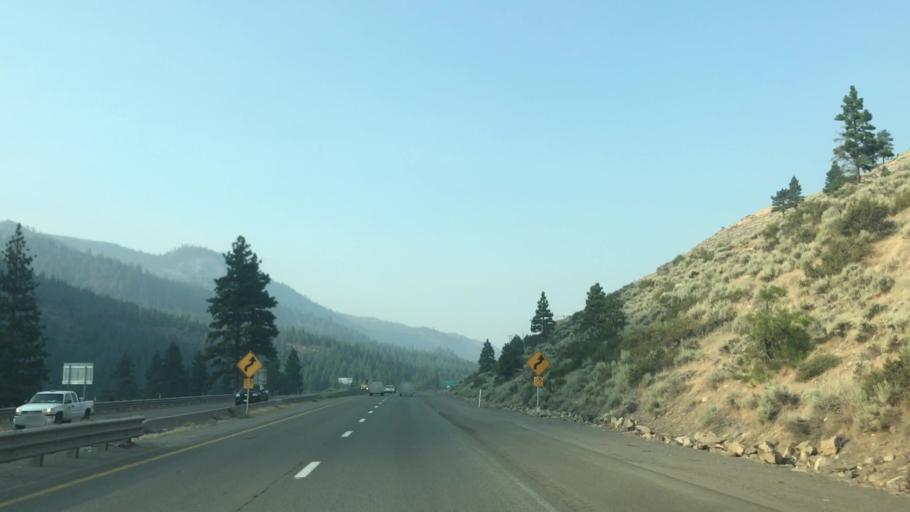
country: US
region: Nevada
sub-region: Washoe County
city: Verdi
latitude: 39.4773
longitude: -119.9959
